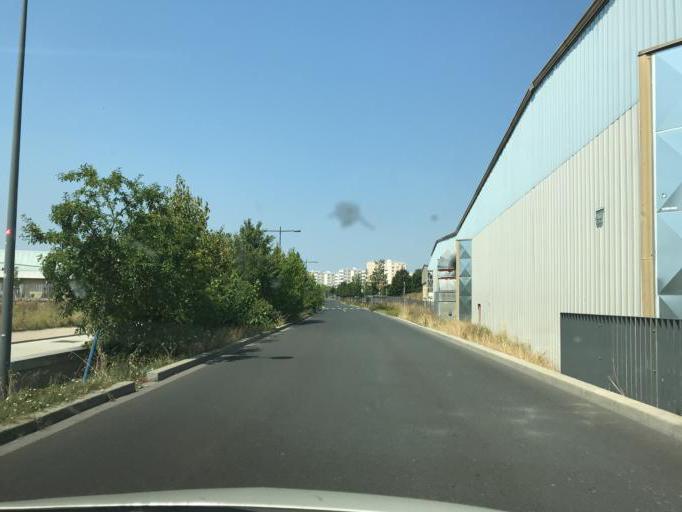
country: FR
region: Rhone-Alpes
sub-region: Departement du Rhone
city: Decines-Charpieu
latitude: 45.7684
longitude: 4.9800
